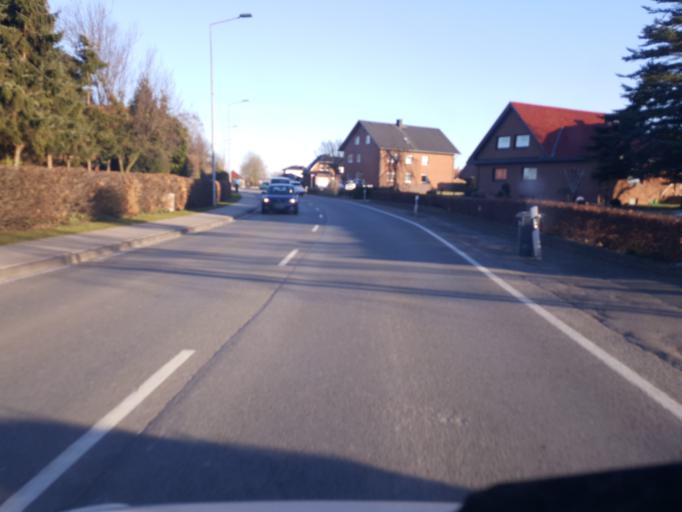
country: DE
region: North Rhine-Westphalia
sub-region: Regierungsbezirk Detmold
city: Hille
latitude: 52.3414
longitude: 8.7370
